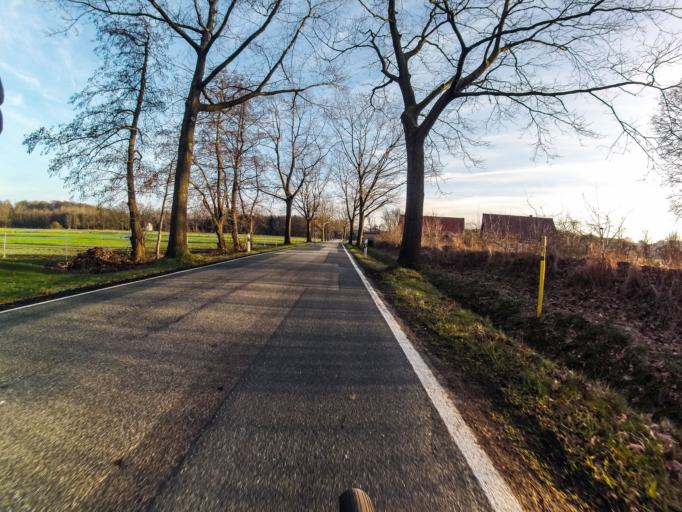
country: DE
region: North Rhine-Westphalia
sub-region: Regierungsbezirk Munster
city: Mettingen
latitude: 52.3004
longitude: 7.8189
